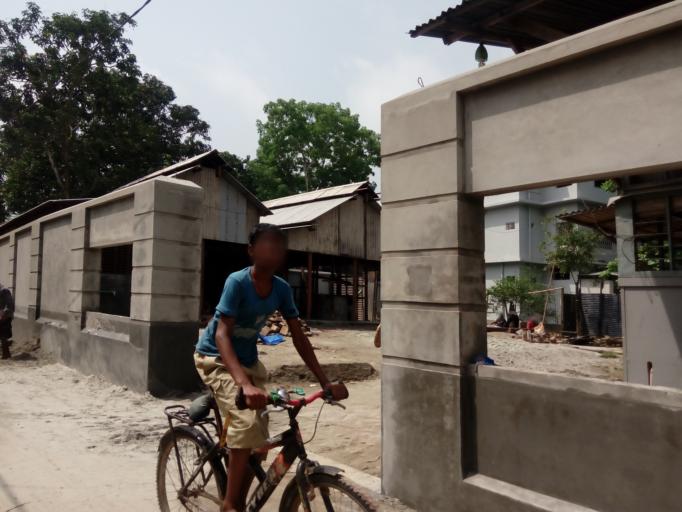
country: BD
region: Rajshahi
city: Sirajganj
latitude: 24.3282
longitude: 89.6862
